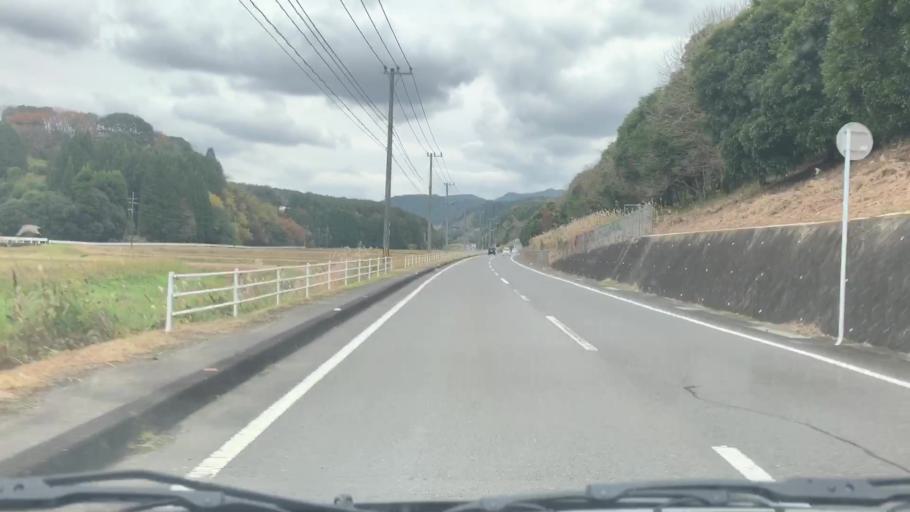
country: JP
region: Saga Prefecture
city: Ureshinomachi-shimojuku
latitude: 33.1237
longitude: 129.9806
